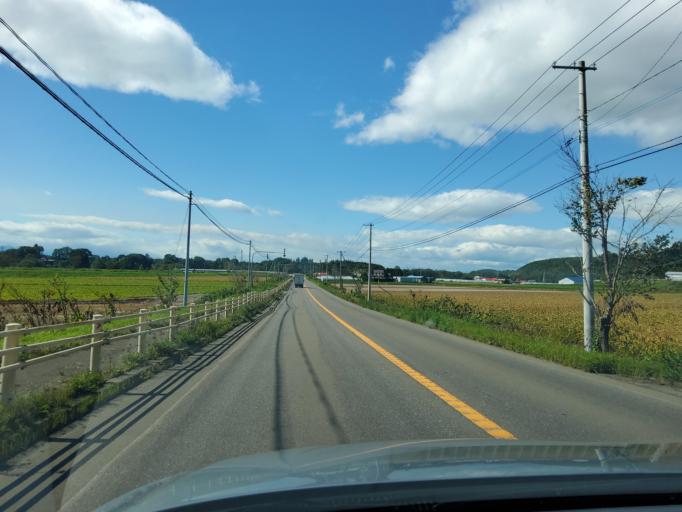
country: JP
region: Hokkaido
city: Obihiro
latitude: 42.9450
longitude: 143.2755
